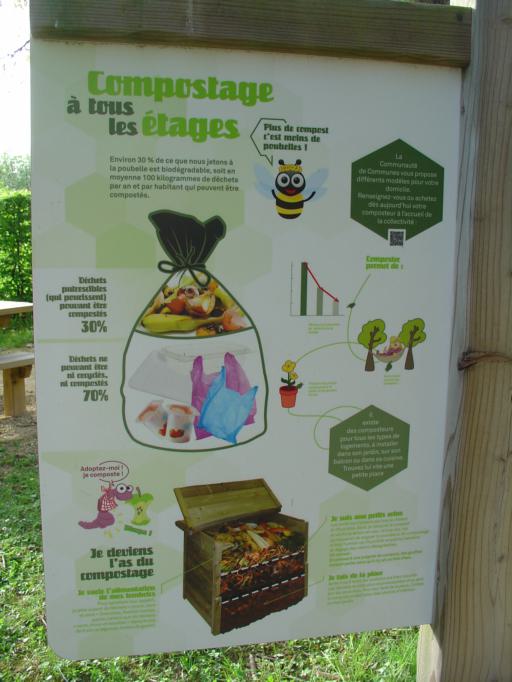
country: FR
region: Lorraine
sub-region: Departement de Meurthe-et-Moselle
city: Ecrouves
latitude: 48.6820
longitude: 5.8618
